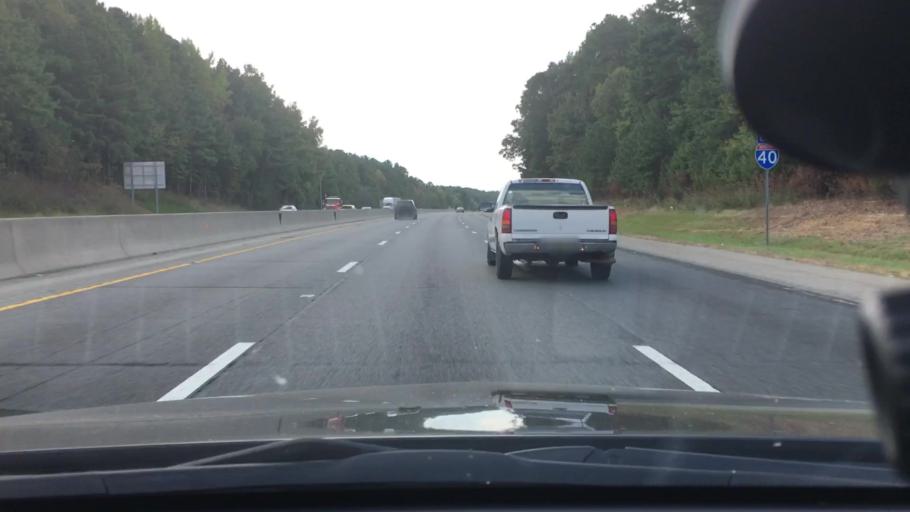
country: US
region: North Carolina
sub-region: Orange County
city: Chapel Hill
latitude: 35.9443
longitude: -78.9940
